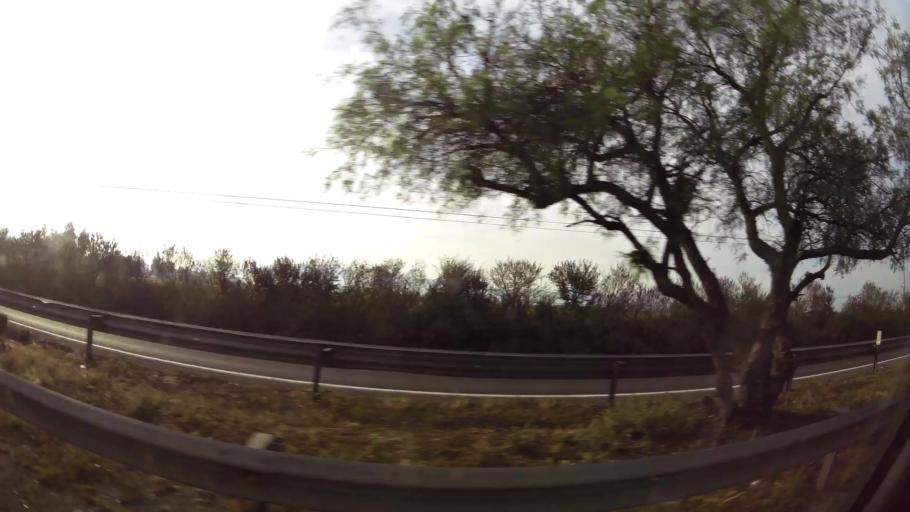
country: CL
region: Santiago Metropolitan
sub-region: Provincia de Talagante
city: Penaflor
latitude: -33.6405
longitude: -70.8738
